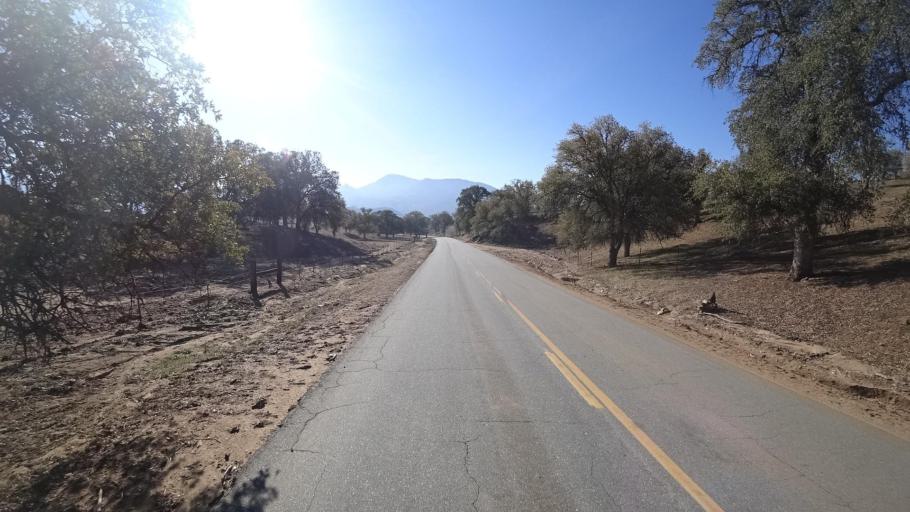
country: US
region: California
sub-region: Kern County
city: Tehachapi
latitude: 35.3289
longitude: -118.3922
